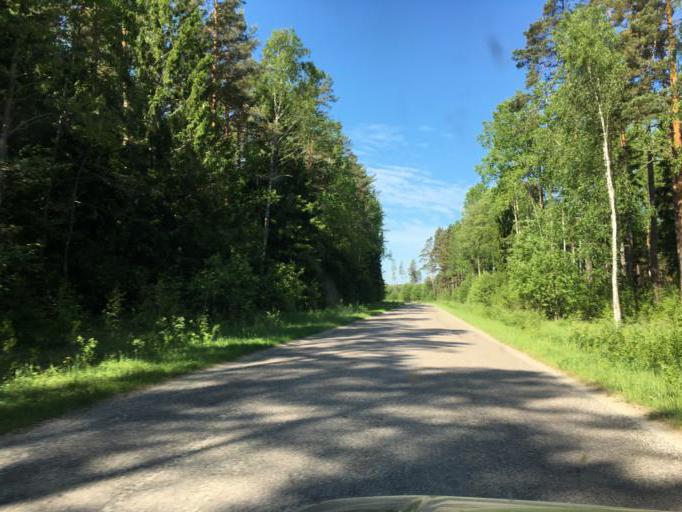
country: LV
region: Ventspils
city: Ventspils
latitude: 57.4922
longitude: 21.8016
